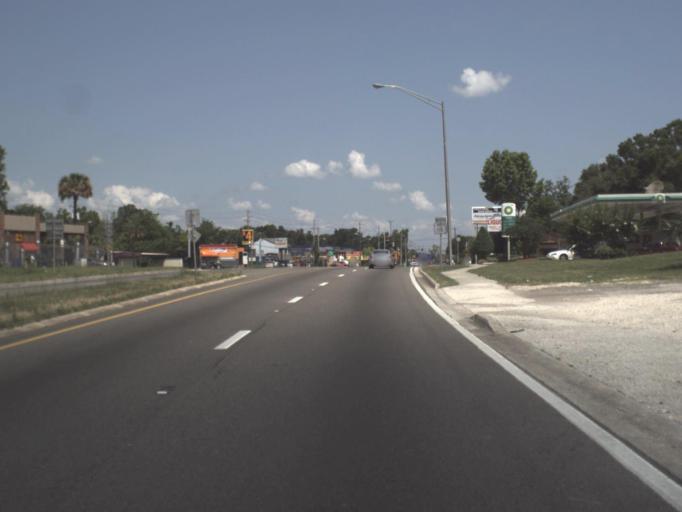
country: US
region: Florida
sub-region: Duval County
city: Jacksonville
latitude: 30.3836
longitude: -81.6736
